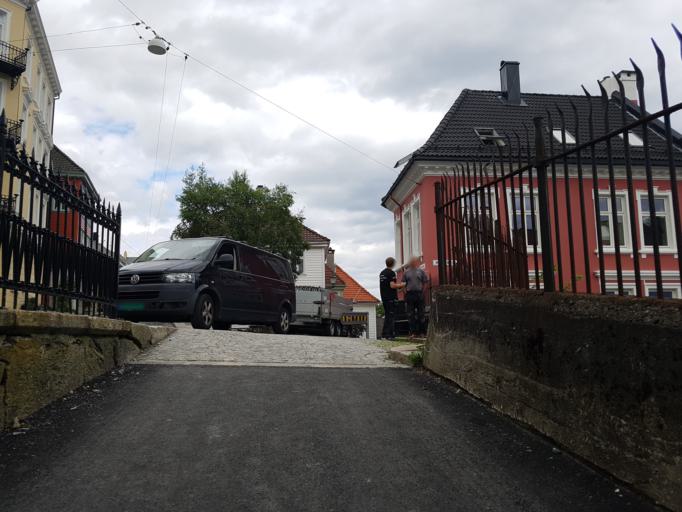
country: NO
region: Hordaland
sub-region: Bergen
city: Bergen
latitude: 60.3895
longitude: 5.3180
